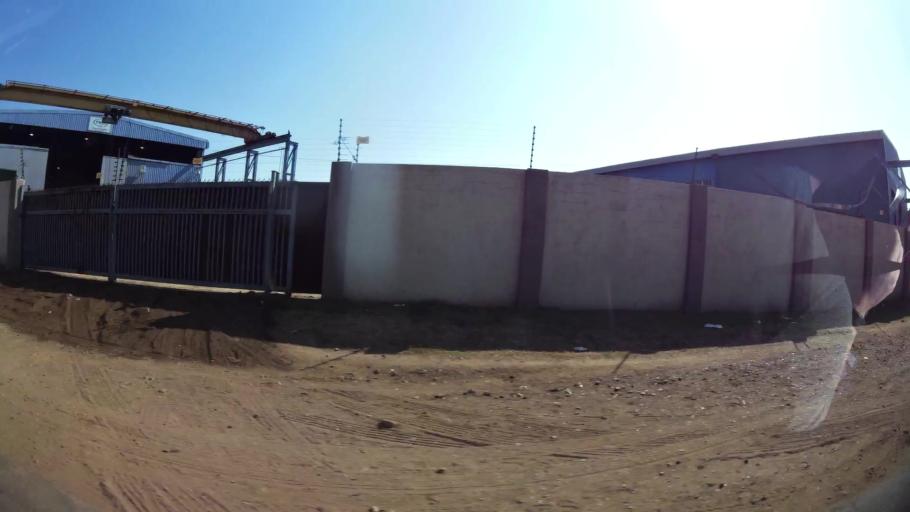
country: ZA
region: Gauteng
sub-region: Ekurhuleni Metropolitan Municipality
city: Boksburg
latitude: -26.1591
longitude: 28.2184
